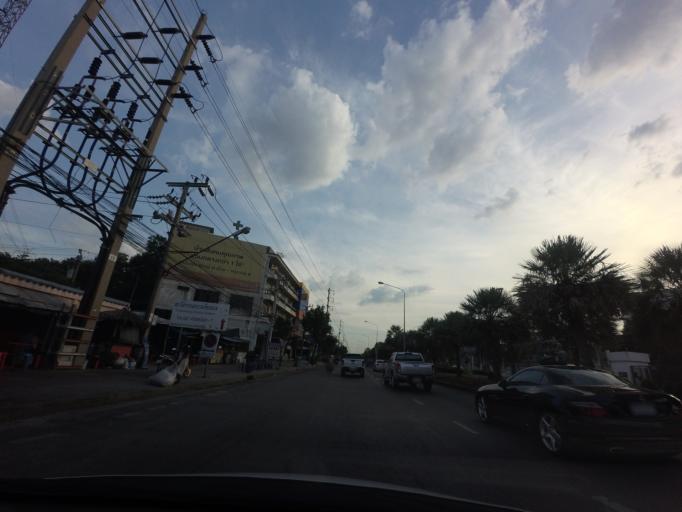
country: TH
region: Bangkok
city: Bang Khun Thian
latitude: 13.6480
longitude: 100.4313
